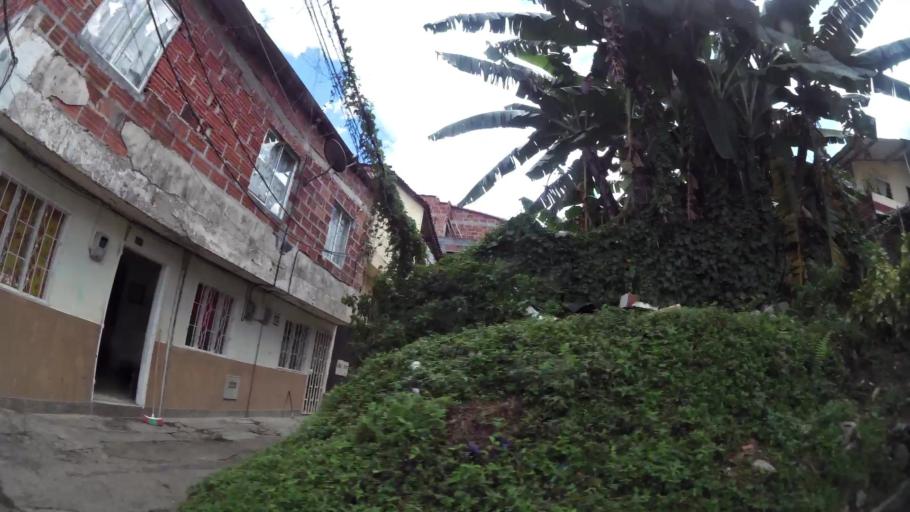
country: CO
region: Antioquia
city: Sabaneta
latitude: 6.1400
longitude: -75.6210
